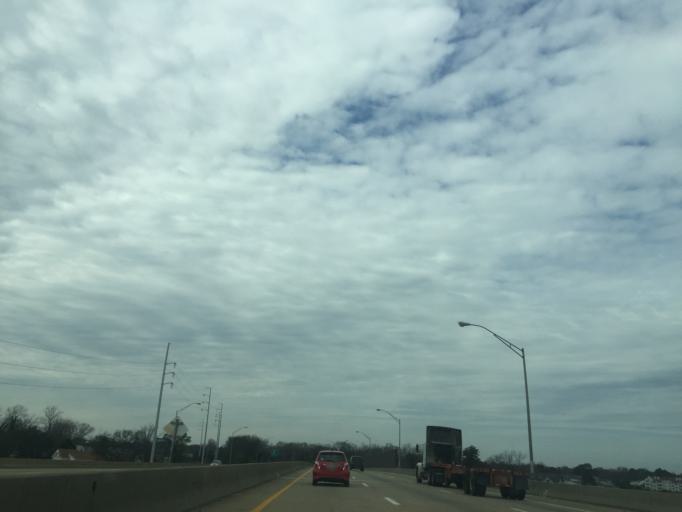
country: US
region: Virginia
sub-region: City of Hampton
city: East Hampton
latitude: 37.0310
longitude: -76.3367
